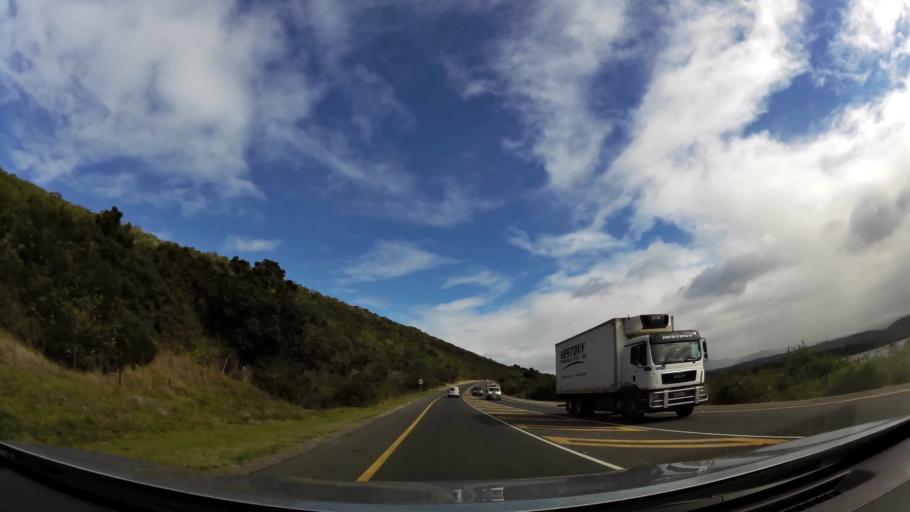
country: ZA
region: Western Cape
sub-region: Eden District Municipality
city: Knysna
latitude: -34.0094
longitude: 22.7533
